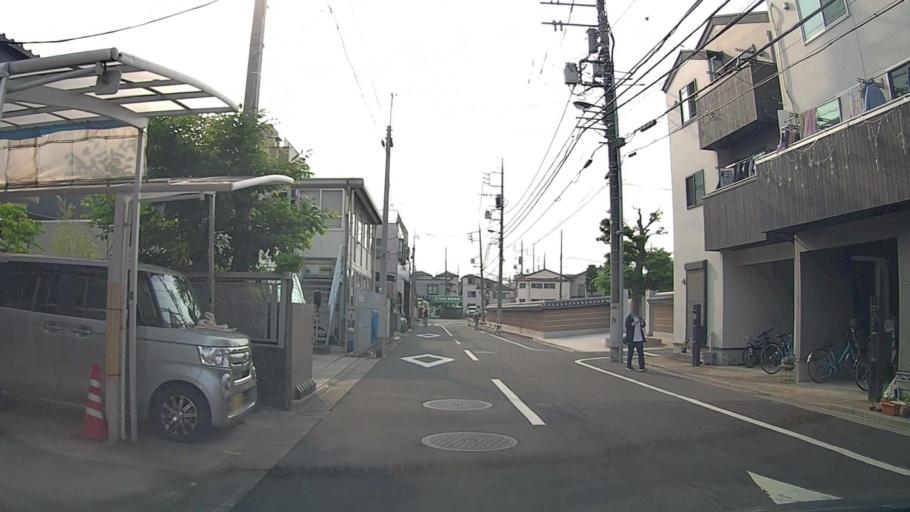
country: JP
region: Saitama
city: Kawaguchi
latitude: 35.7587
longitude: 139.7600
